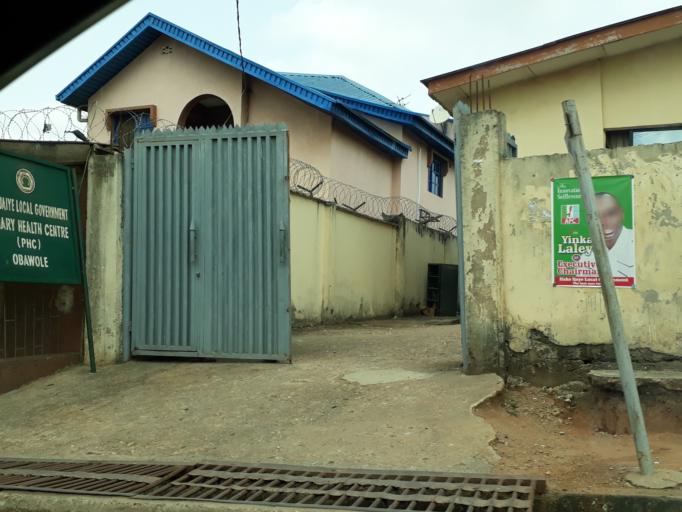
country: NG
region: Lagos
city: Ifako
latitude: 6.6565
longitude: 3.3332
